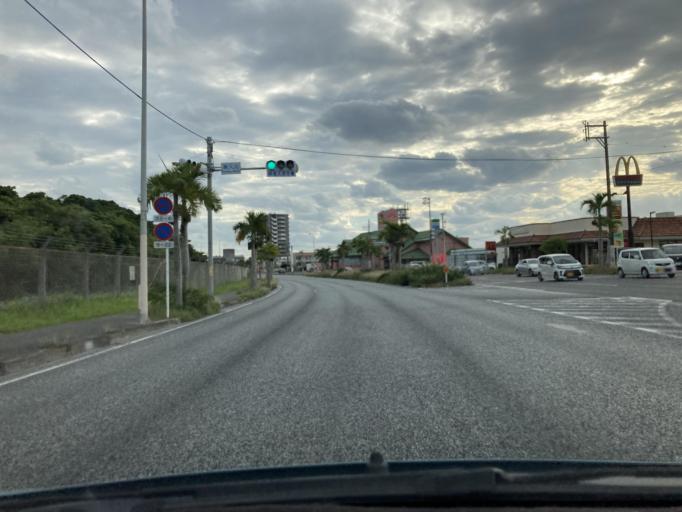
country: JP
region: Okinawa
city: Chatan
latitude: 26.3573
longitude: 127.7462
